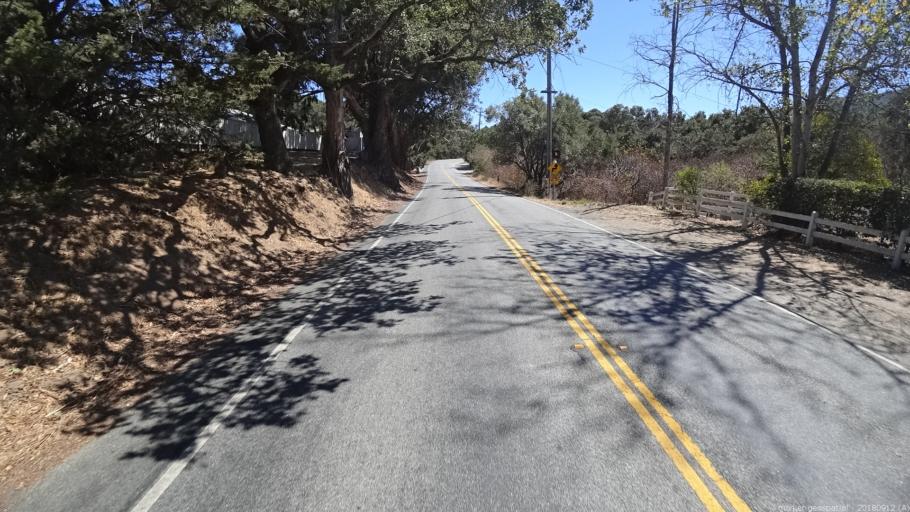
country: US
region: California
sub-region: Monterey County
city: Carmel Valley Village
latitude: 36.4932
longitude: -121.7454
